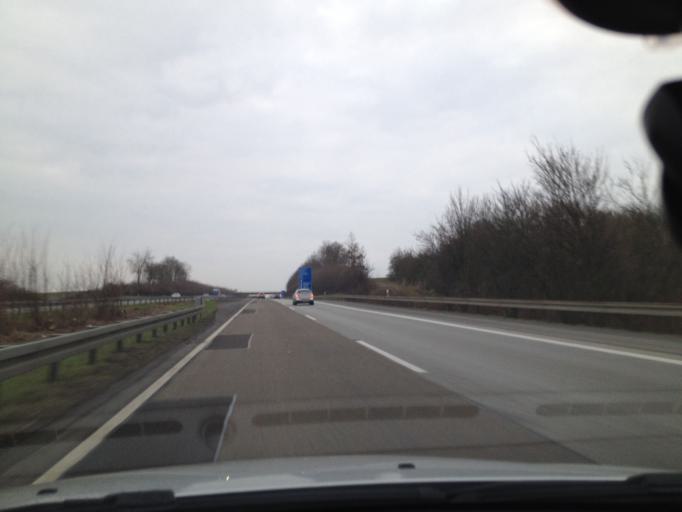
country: DE
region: Hesse
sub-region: Regierungsbezirk Darmstadt
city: Munzenberg
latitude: 50.4723
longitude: 8.7498
